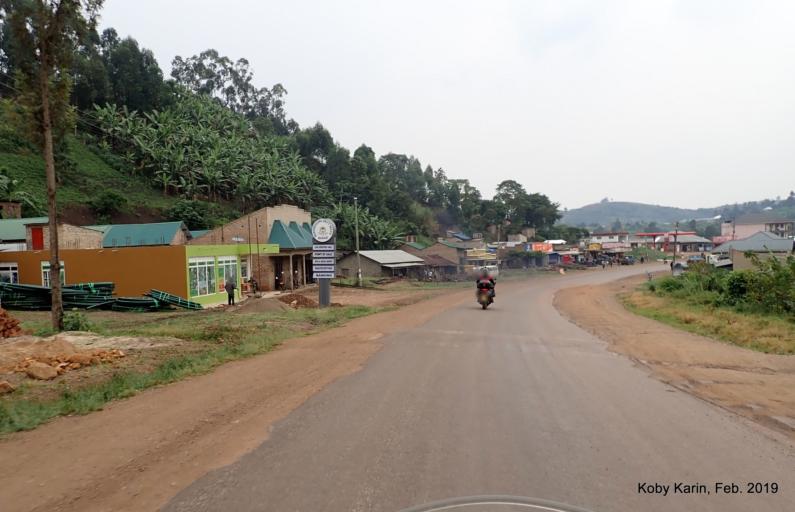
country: UG
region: Western Region
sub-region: Rubirizi District
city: Rubirizi
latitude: -0.2625
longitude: 30.1057
